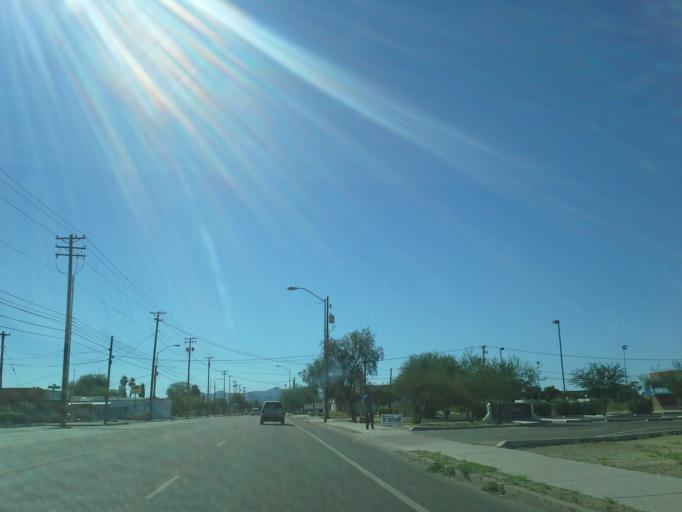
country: US
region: Arizona
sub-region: Pima County
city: Tucson
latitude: 32.2505
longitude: -110.9213
